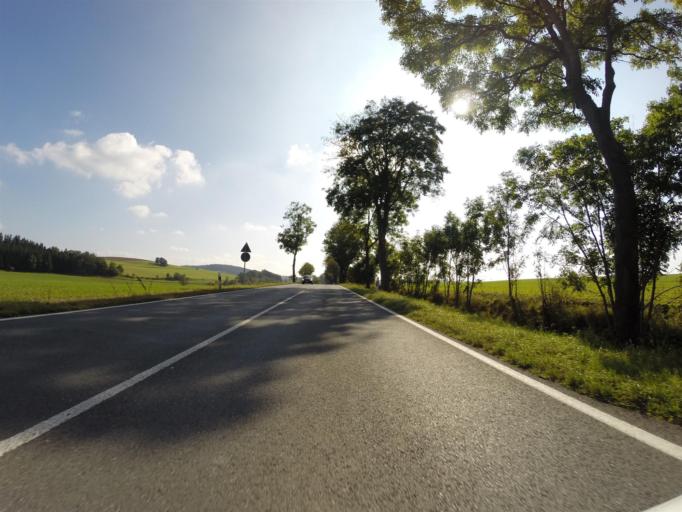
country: DE
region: Thuringia
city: Tanna
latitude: 50.5244
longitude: 11.8233
